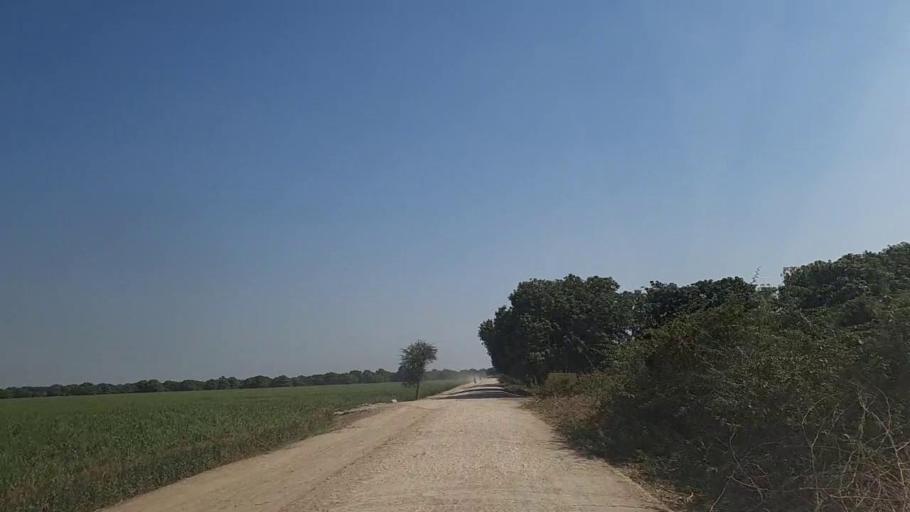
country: PK
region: Sindh
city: Digri
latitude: 25.1703
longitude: 69.2035
